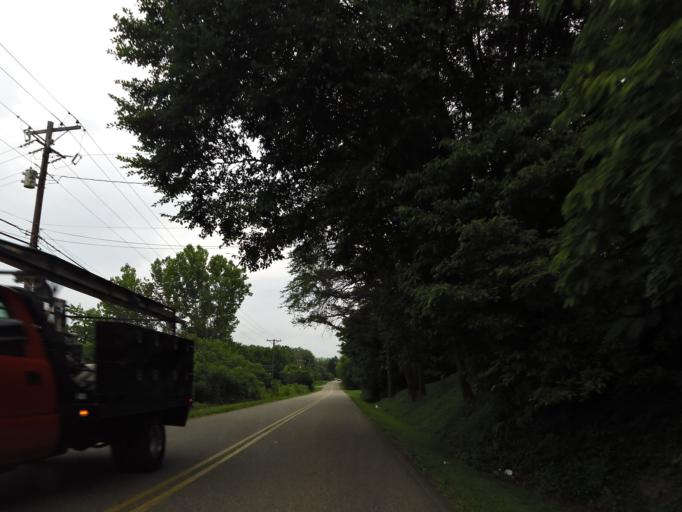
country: US
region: Tennessee
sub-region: Sevier County
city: Seymour
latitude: 35.9160
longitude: -83.8261
